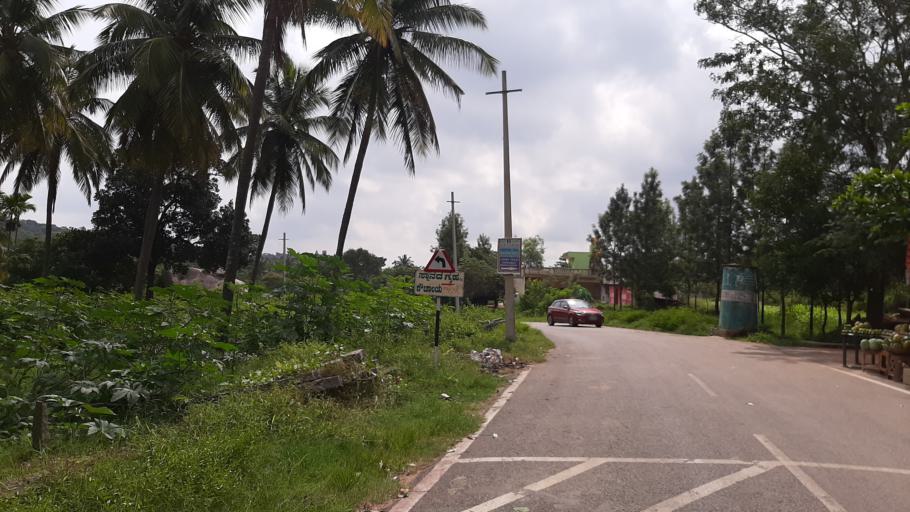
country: IN
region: Karnataka
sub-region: Ramanagara
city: Magadi
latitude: 12.9018
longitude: 77.2862
